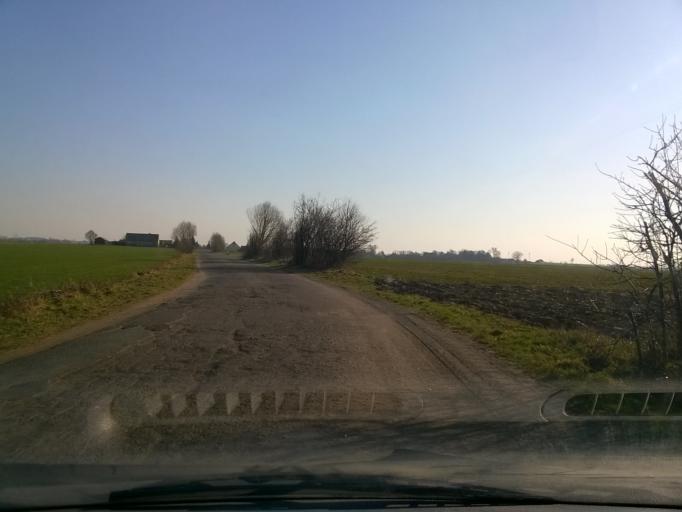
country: PL
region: Greater Poland Voivodeship
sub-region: Powiat wagrowiecki
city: Golancz
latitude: 52.9731
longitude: 17.3355
